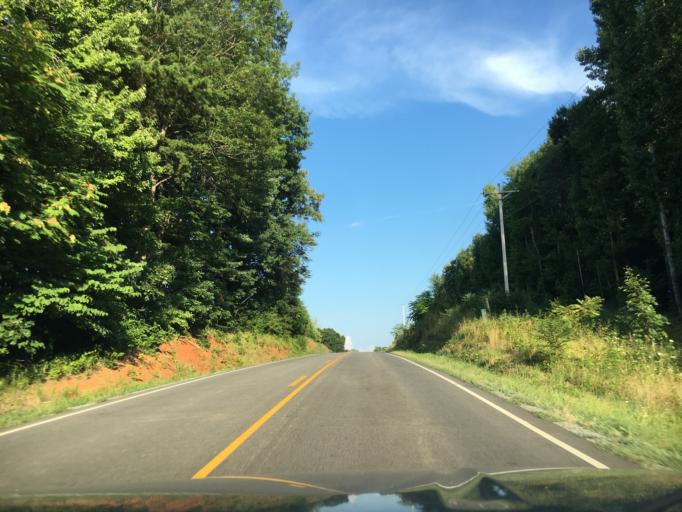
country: US
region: Virginia
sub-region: Franklin County
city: Union Hall
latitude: 36.9614
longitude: -79.5751
